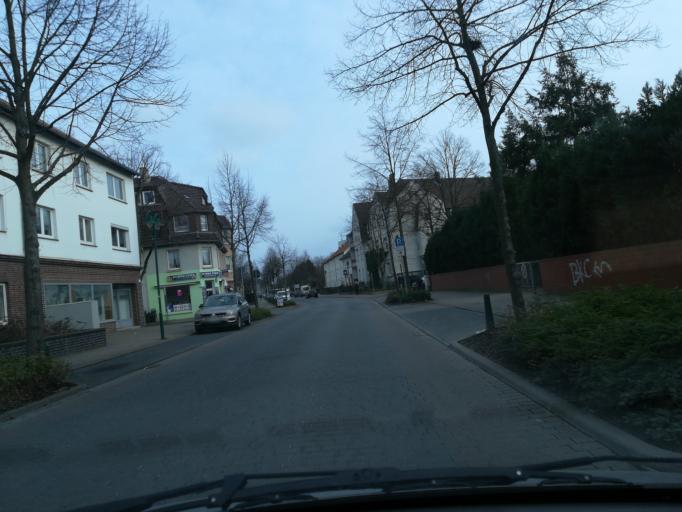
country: DE
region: Lower Saxony
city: Seelze
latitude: 52.3950
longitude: 9.5958
